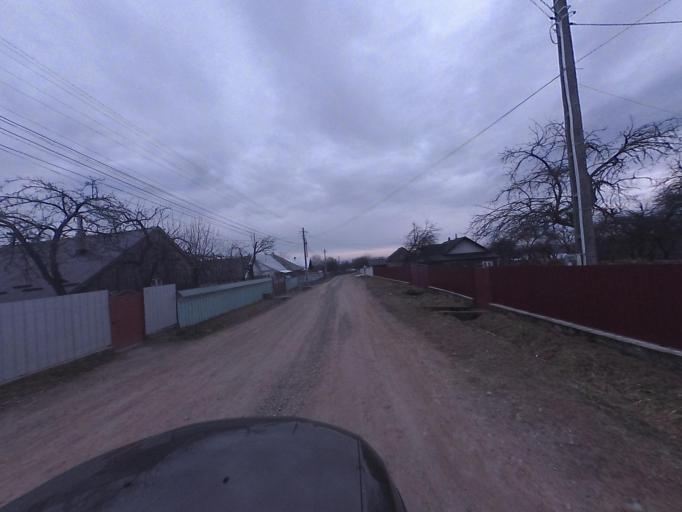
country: RO
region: Neamt
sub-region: Oras Targu Neamt
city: Humulesti
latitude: 47.1899
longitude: 26.3388
